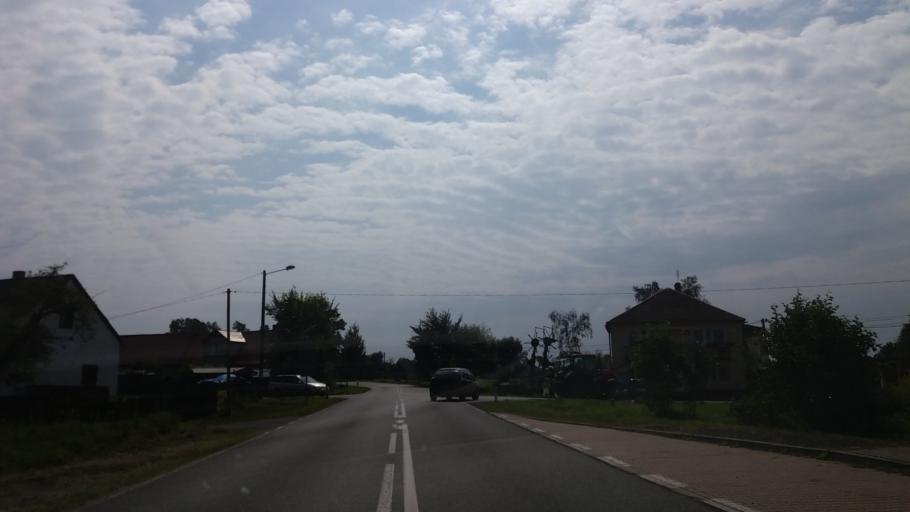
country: PL
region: Lubusz
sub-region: Powiat strzelecko-drezdenecki
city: Stare Kurowo
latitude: 52.7910
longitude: 15.6379
